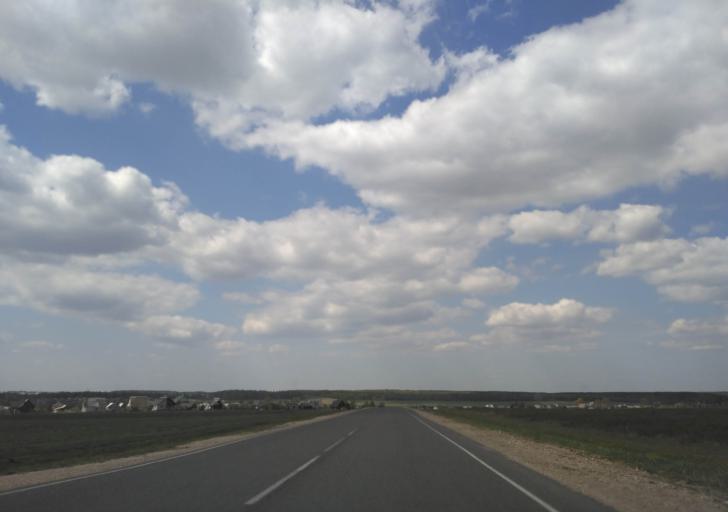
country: BY
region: Minsk
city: Vilyeyka
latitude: 54.5149
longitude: 26.9867
